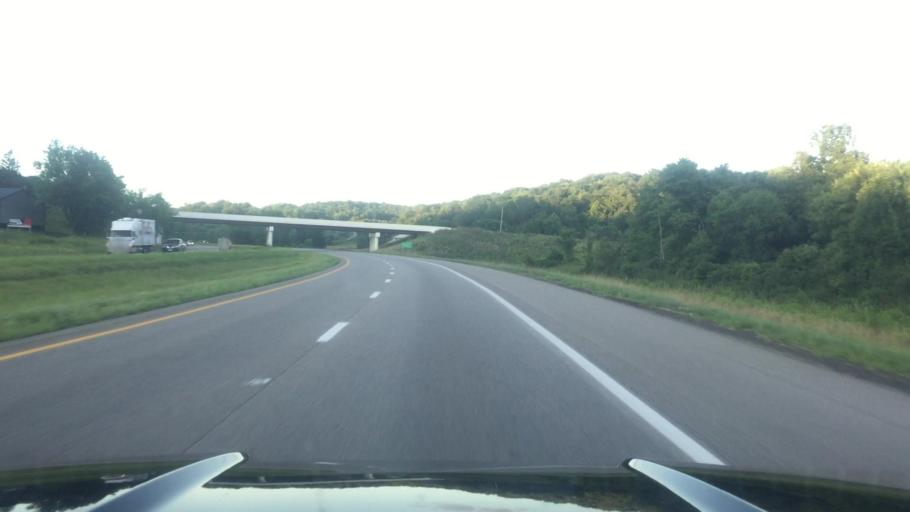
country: US
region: Ohio
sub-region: Tuscarawas County
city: Strasburg
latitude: 40.5929
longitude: -81.5129
